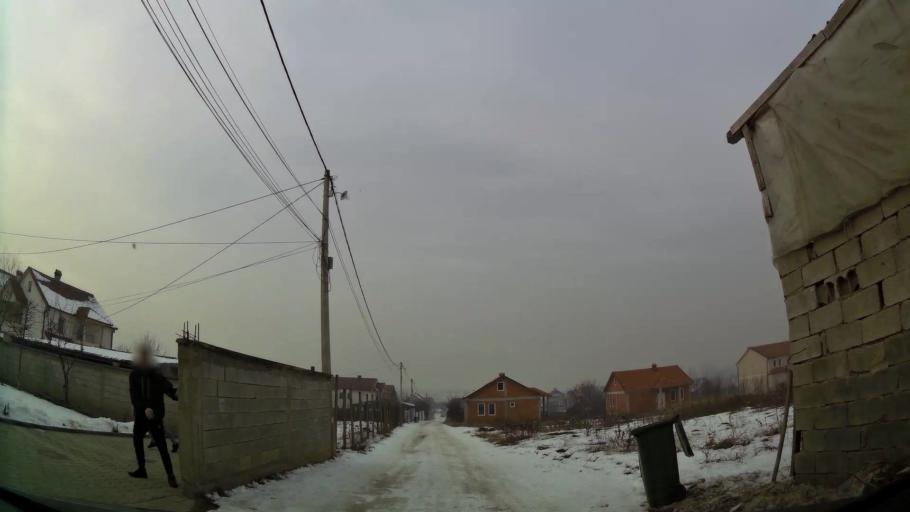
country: MK
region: Suto Orizari
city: Suto Orizare
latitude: 42.0372
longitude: 21.4163
